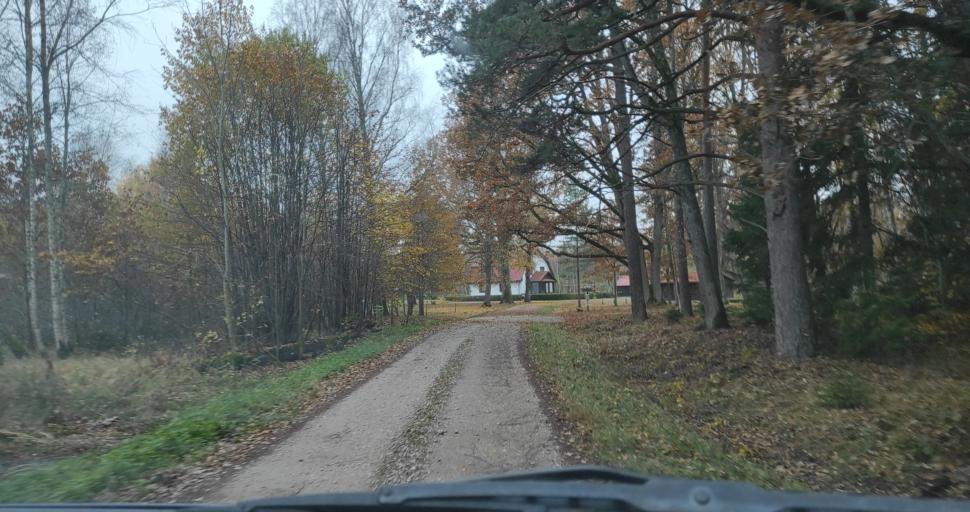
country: LV
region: Durbe
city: Liegi
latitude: 56.7509
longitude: 21.3485
